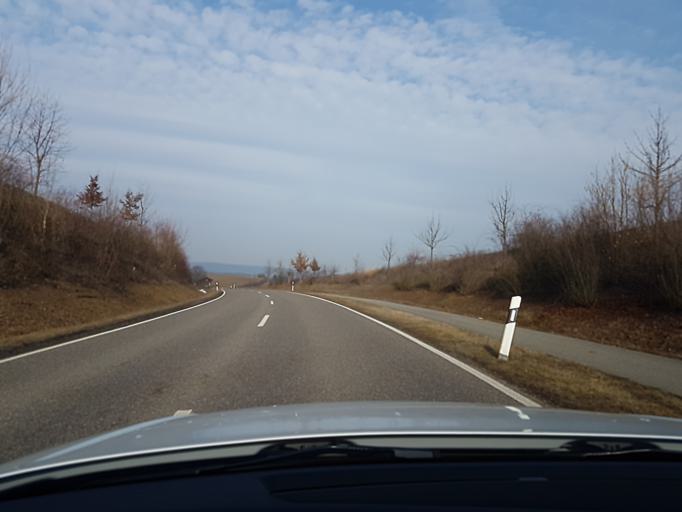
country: DE
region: Baden-Wuerttemberg
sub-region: Regierungsbezirk Stuttgart
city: Lauffen am Neckar
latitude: 49.0859
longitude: 9.1461
